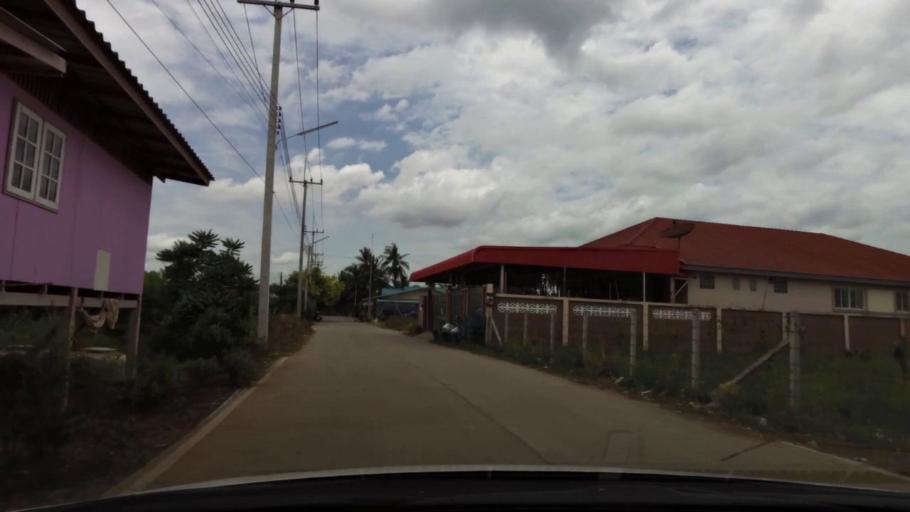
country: TH
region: Samut Sakhon
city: Ban Phaeo
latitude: 13.5689
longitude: 100.0354
